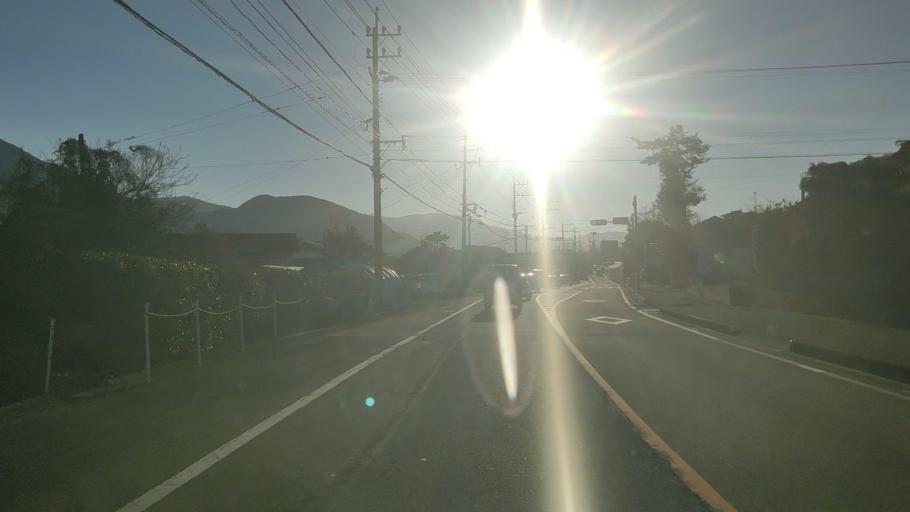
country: JP
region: Miyazaki
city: Miyazaki-shi
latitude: 31.8478
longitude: 131.3495
